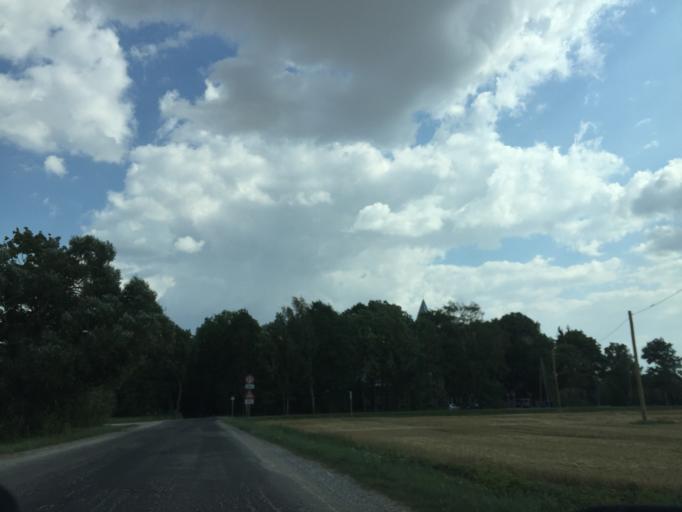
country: LV
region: Jelgava
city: Jelgava
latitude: 56.5116
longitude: 23.7549
